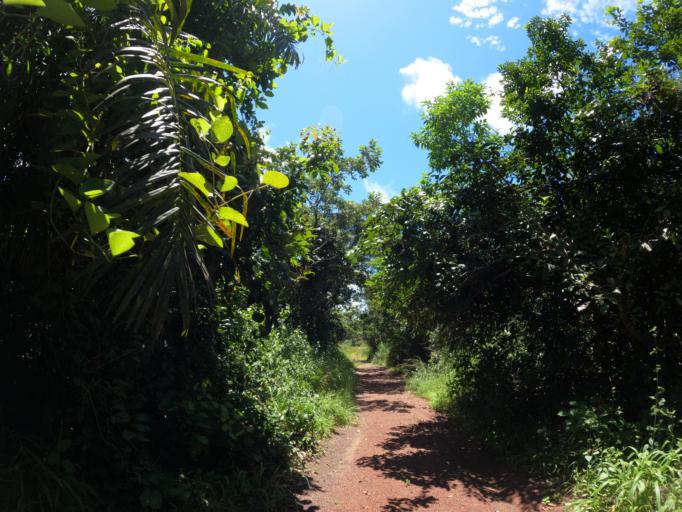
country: SL
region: Northern Province
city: Makeni
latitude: 9.0692
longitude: -12.2761
